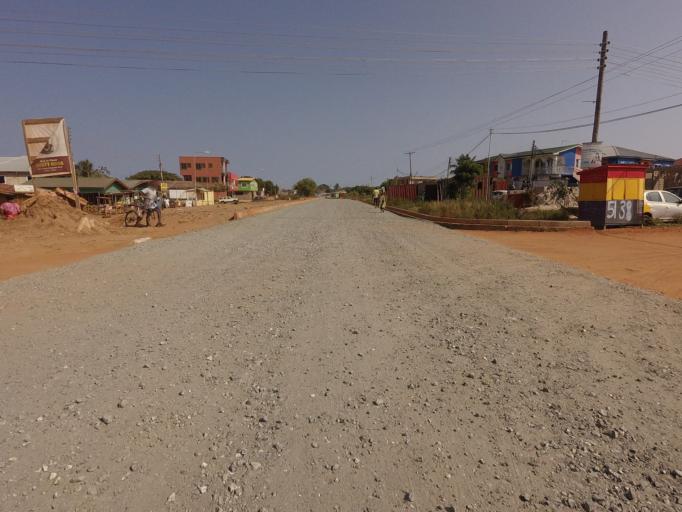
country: GH
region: Greater Accra
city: Teshi Old Town
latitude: 5.5917
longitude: -0.1162
